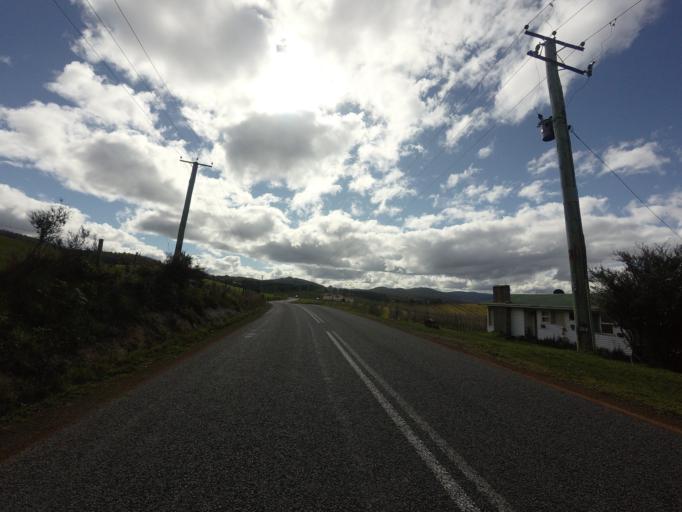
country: AU
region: Tasmania
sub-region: Huon Valley
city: Geeveston
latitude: -43.2089
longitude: 146.9756
